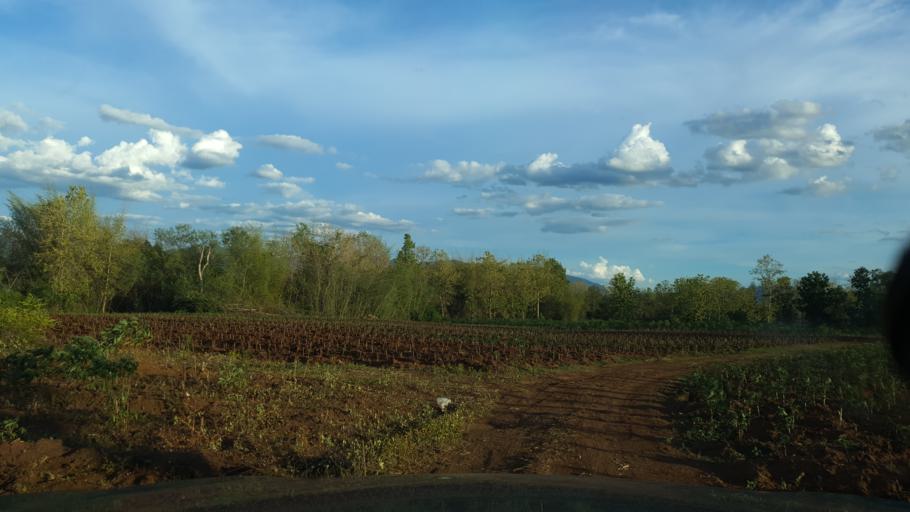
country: TH
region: Lampang
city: Sop Prap
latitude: 17.9615
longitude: 99.3521
